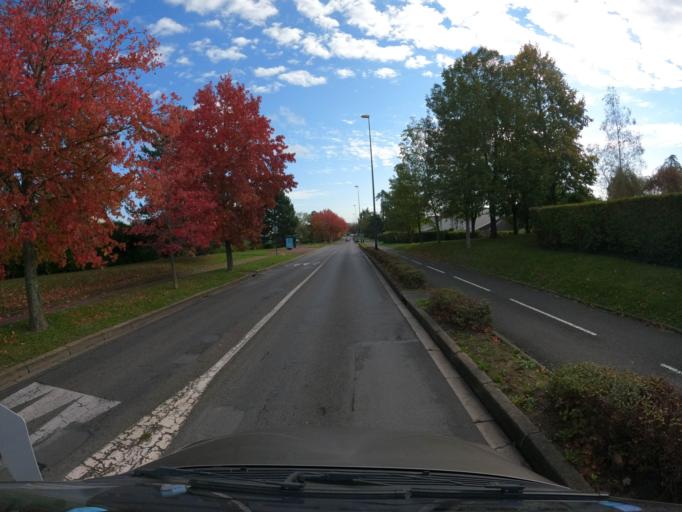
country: FR
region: Ile-de-France
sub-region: Departement de Seine-et-Marne
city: Chelles
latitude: 48.8836
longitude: 2.6059
